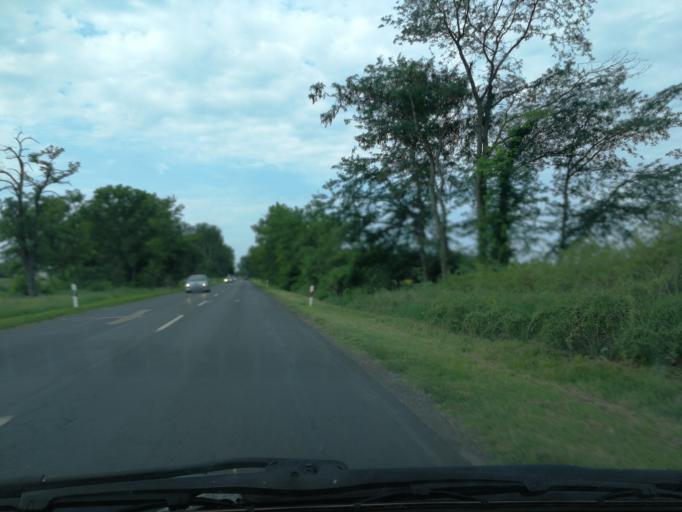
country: HU
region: Bacs-Kiskun
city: Ersekcsanad
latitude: 46.2215
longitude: 18.9654
